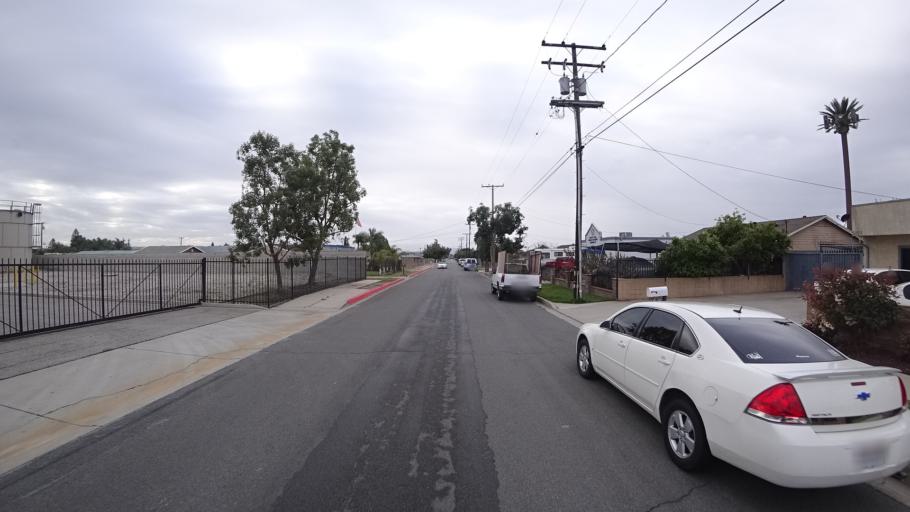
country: US
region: California
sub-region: Los Angeles County
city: Irwindale
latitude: 34.1054
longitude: -117.9463
